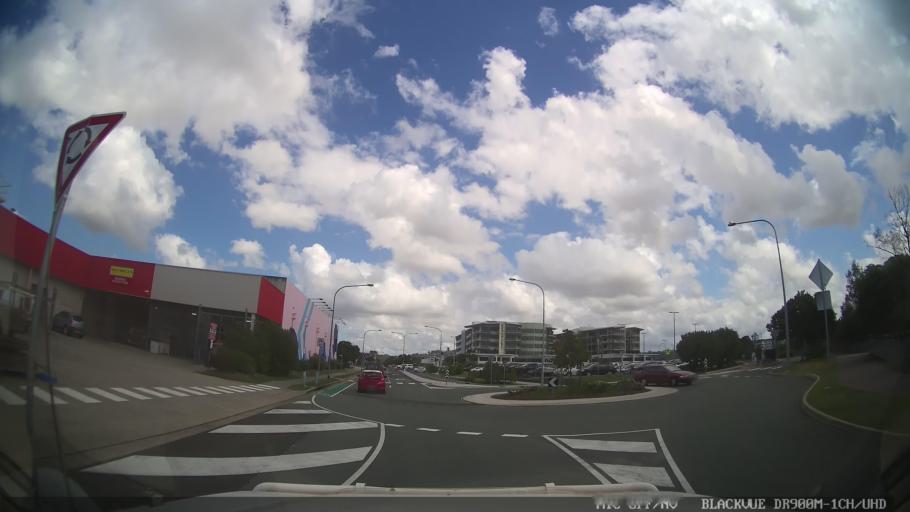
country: AU
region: Queensland
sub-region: Sunshine Coast
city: Buderim
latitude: -26.6561
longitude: 153.0854
